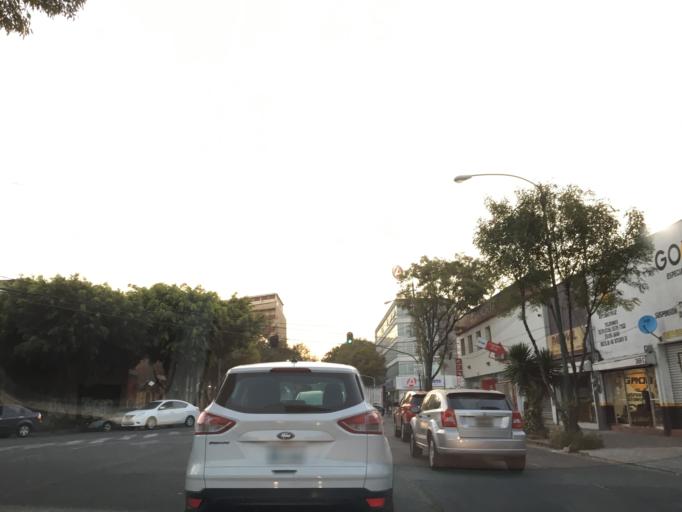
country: MX
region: Mexico City
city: Mexico City
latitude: 19.4202
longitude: -99.1397
